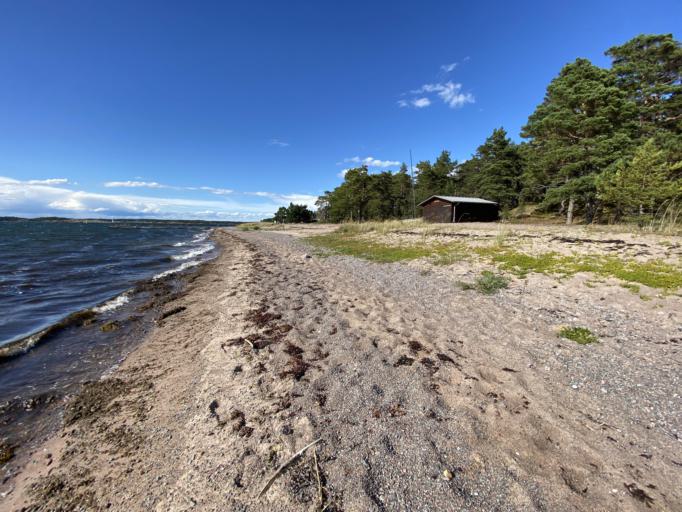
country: SE
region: Stockholm
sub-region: Varmdo Kommun
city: Holo
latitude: 59.2820
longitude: 18.9010
